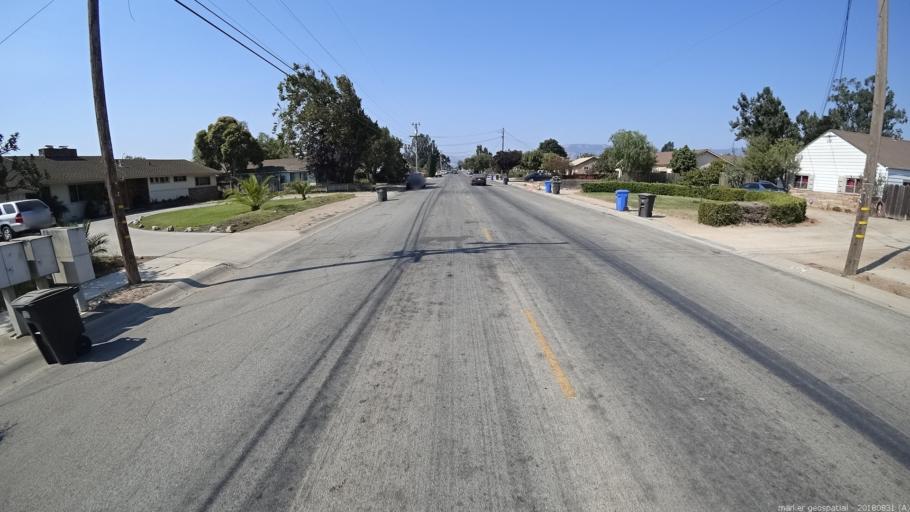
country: US
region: California
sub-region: Monterey County
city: Greenfield
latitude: 36.3253
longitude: -121.2354
